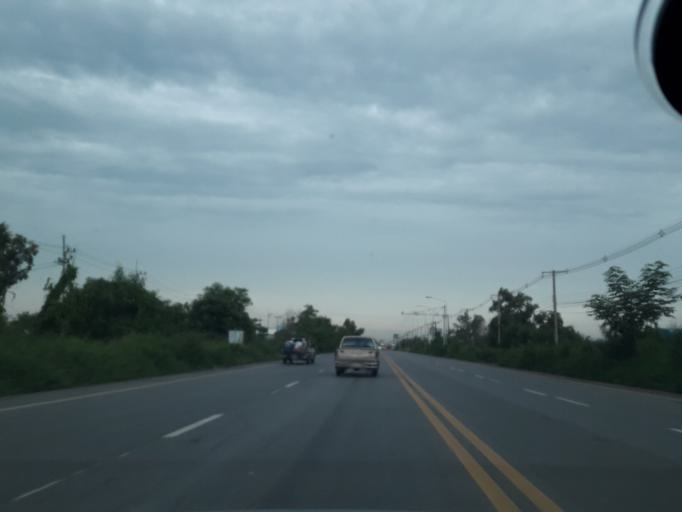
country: TH
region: Pathum Thani
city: Ban Rangsit
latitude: 14.0659
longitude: 100.7471
